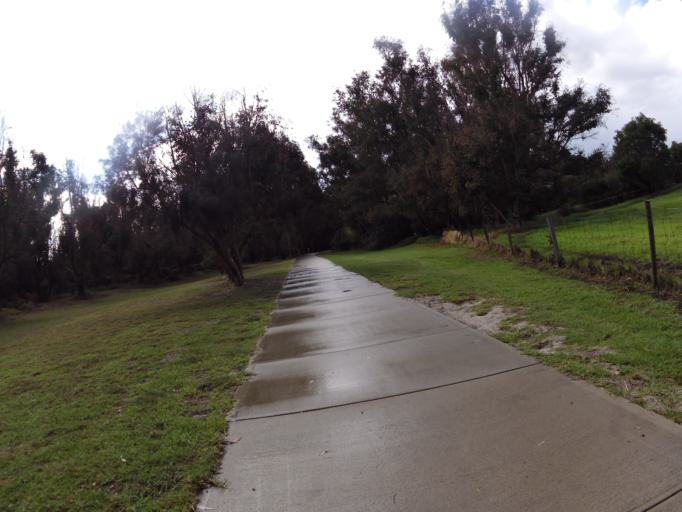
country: AU
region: Western Australia
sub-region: Donnybrook-Balingup
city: Donnybrook
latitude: -33.5729
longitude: 115.8258
